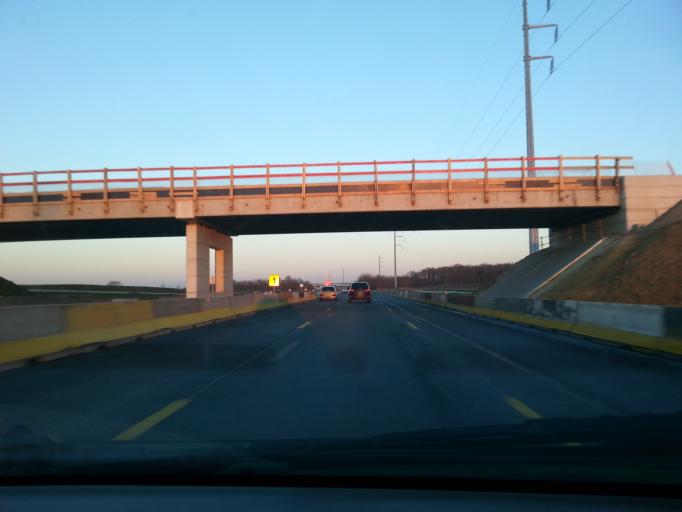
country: FR
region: Centre
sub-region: Departement d'Eure-et-Loir
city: Bailleau-le-Pin
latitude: 48.2915
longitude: 1.2717
